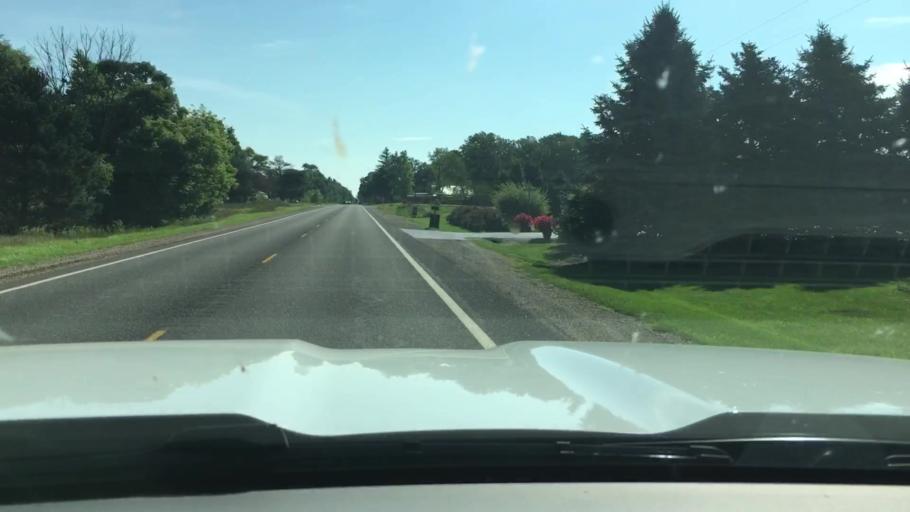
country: US
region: Michigan
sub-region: Montcalm County
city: Edmore
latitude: 43.4083
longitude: -84.8681
